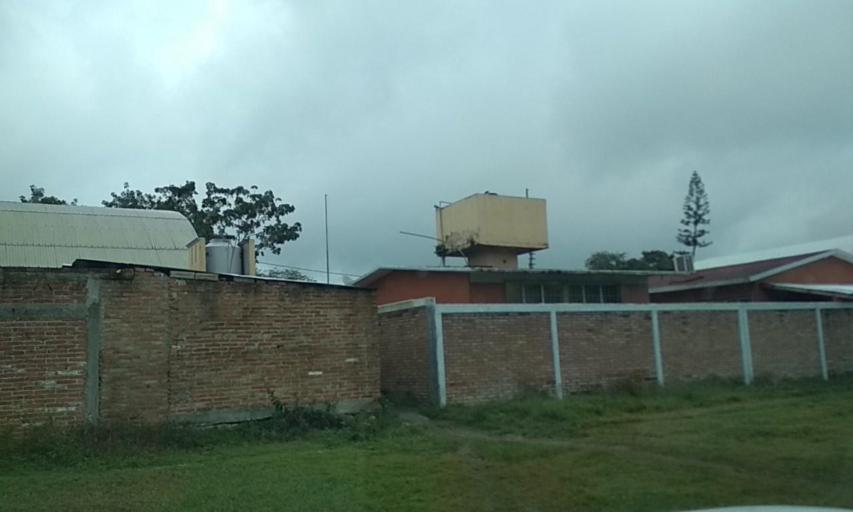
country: MX
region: Veracruz
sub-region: Papantla
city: El Chote
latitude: 20.3722
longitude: -97.3345
